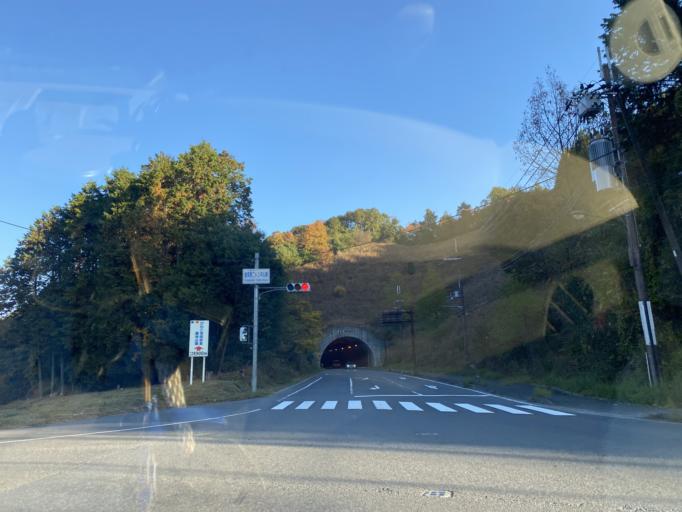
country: JP
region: Kyoto
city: Uji
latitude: 34.9013
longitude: 135.8826
